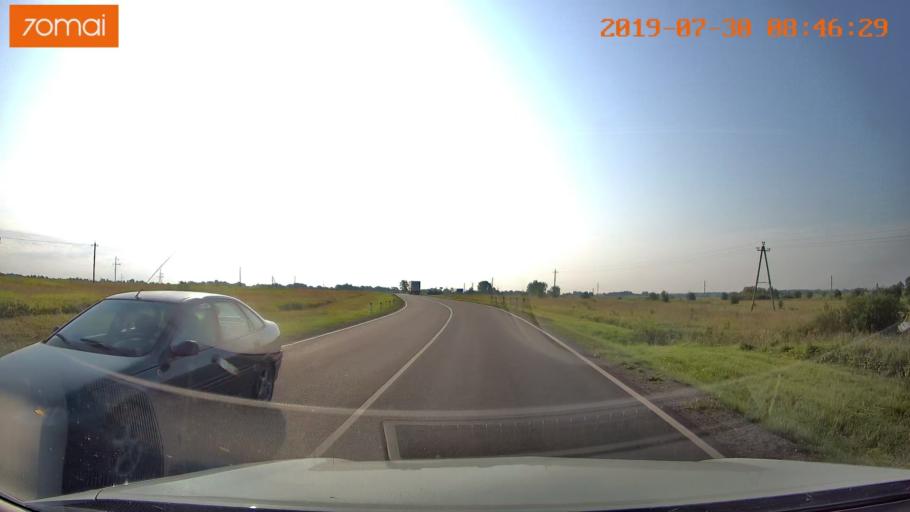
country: RU
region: Kaliningrad
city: Chernyakhovsk
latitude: 54.6229
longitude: 21.8853
